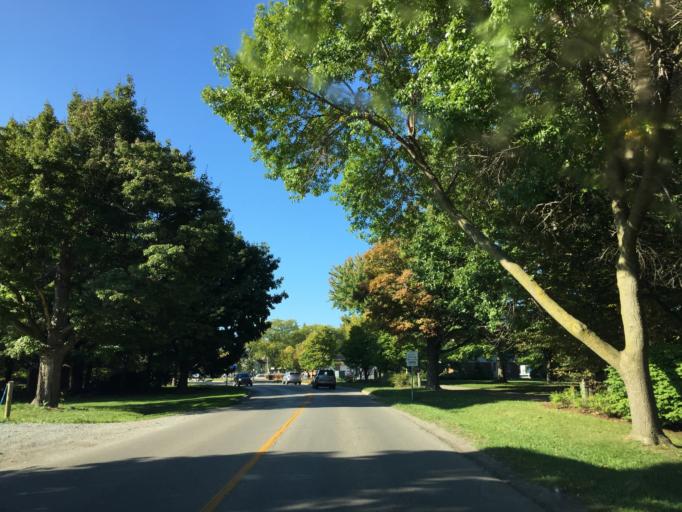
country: US
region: New York
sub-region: Niagara County
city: Youngstown
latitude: 43.2519
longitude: -79.0662
